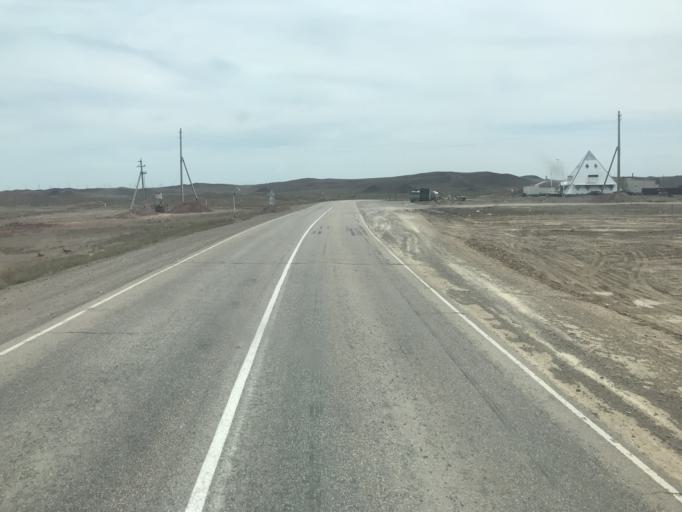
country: KZ
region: Zhambyl
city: Mynaral
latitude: 45.4519
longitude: 73.6002
